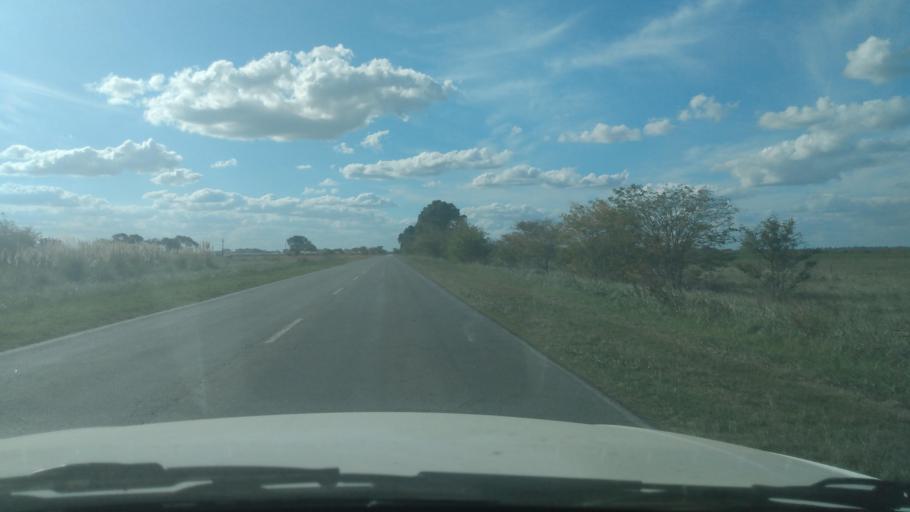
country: AR
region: Buenos Aires
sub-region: Partido de Navarro
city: Navarro
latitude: -34.9814
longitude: -59.3161
